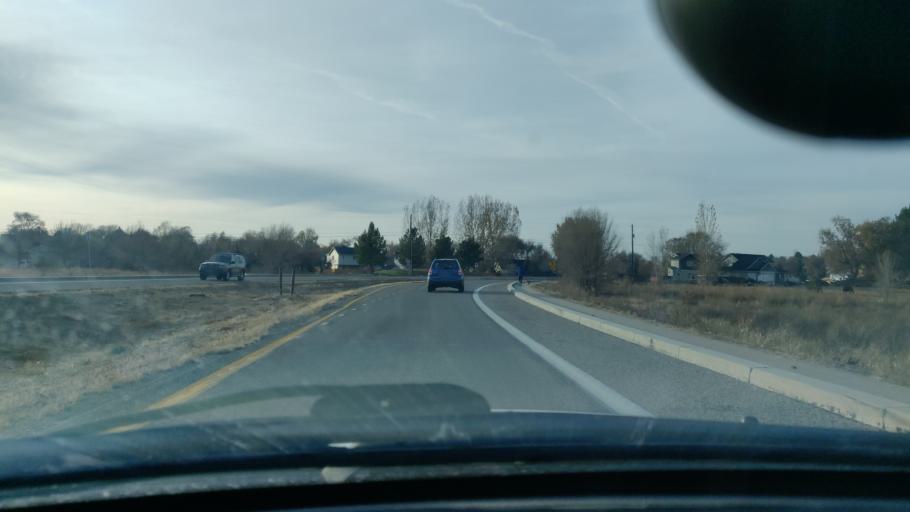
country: US
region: Idaho
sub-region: Ada County
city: Eagle
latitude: 43.6866
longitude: -116.2998
